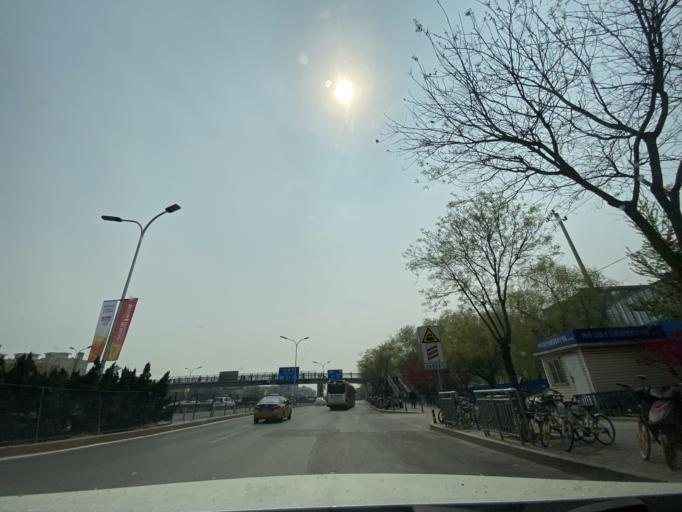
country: CN
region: Beijing
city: Sijiqing
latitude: 39.9414
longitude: 116.2678
